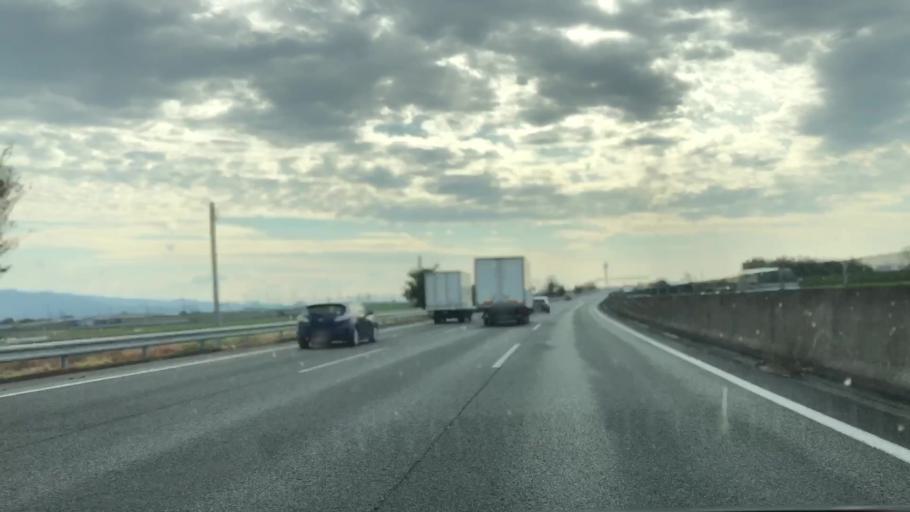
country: JP
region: Saga Prefecture
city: Tosu
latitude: 33.3616
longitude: 130.5407
